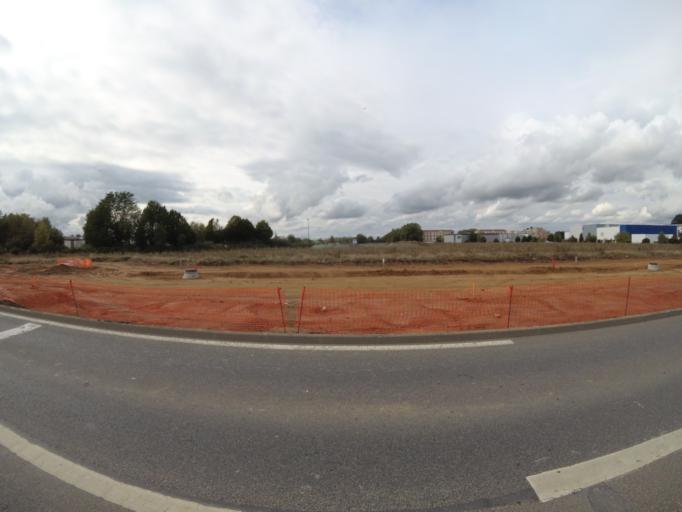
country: FR
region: Ile-de-France
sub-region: Departement de Seine-et-Marne
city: Montevrain
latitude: 48.8648
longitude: 2.7649
